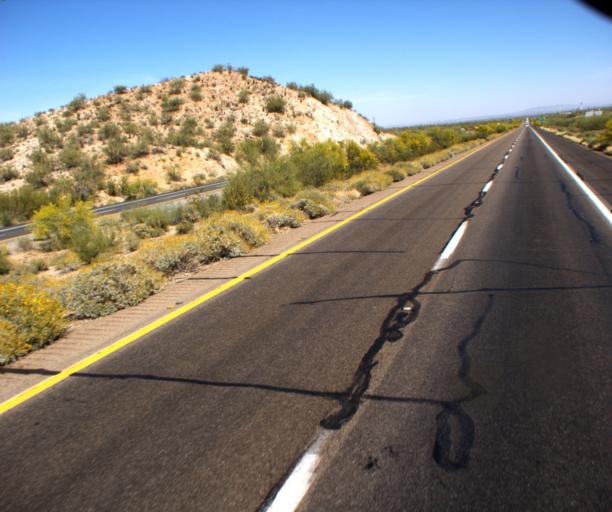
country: US
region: Arizona
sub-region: Pinal County
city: Maricopa
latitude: 32.8348
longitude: -112.1547
